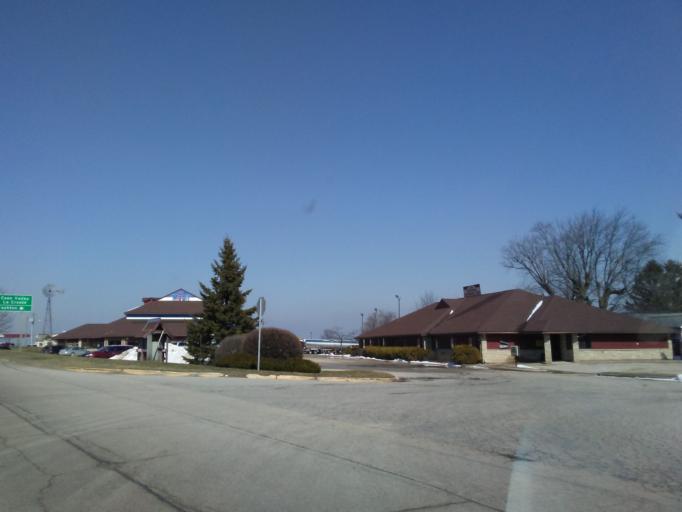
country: US
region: Wisconsin
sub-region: Vernon County
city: Westby
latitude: 43.6580
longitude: -90.8560
